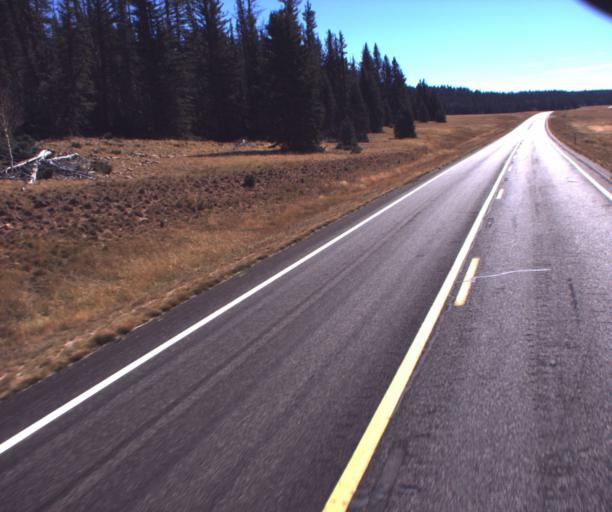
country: US
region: Arizona
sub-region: Coconino County
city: Grand Canyon
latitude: 36.3719
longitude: -112.1232
